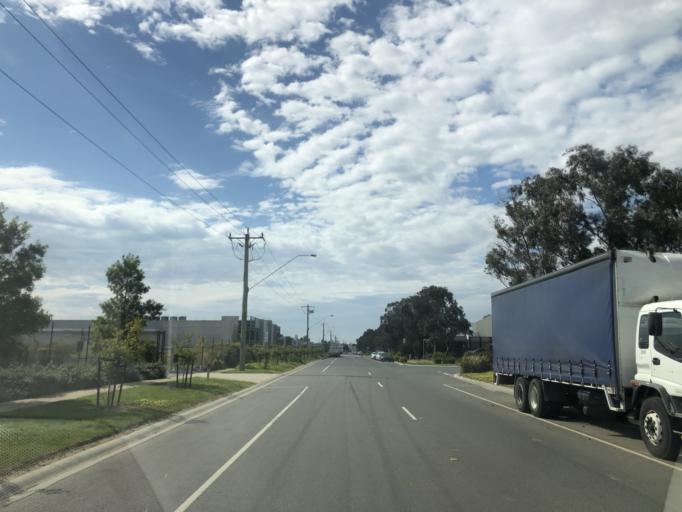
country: AU
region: Victoria
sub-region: Casey
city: Hampton Park
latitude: -38.0390
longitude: 145.2280
